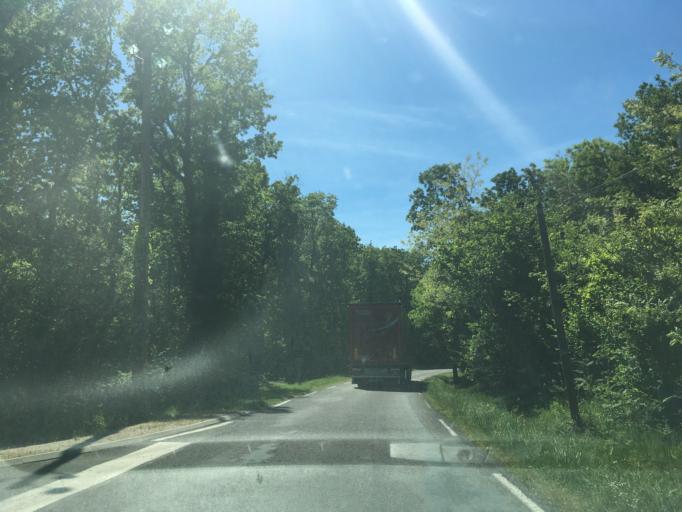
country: FR
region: Aquitaine
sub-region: Departement de la Gironde
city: Lesparre-Medoc
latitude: 45.2655
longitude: -0.8973
